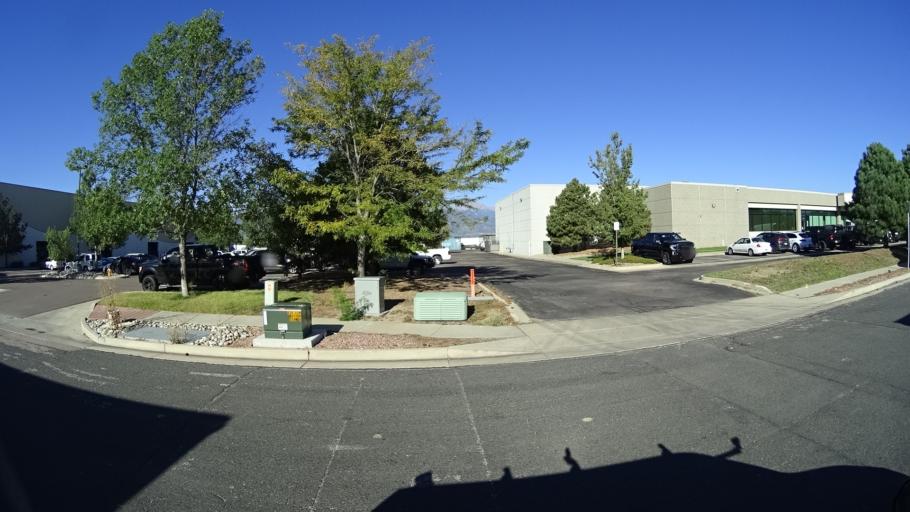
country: US
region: Colorado
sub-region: El Paso County
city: Cimarron Hills
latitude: 38.8110
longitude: -104.7284
